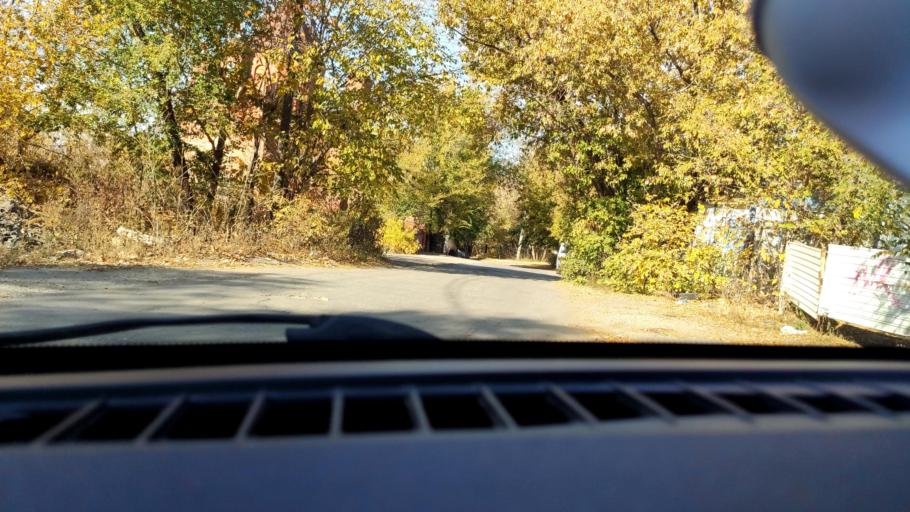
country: RU
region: Samara
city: Samara
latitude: 53.2224
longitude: 50.1653
